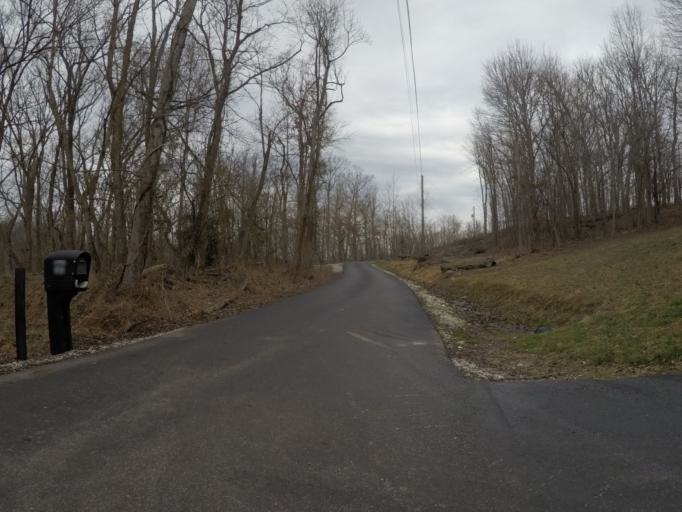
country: US
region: West Virginia
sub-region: Cabell County
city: Pea Ridge
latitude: 38.3935
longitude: -82.3750
